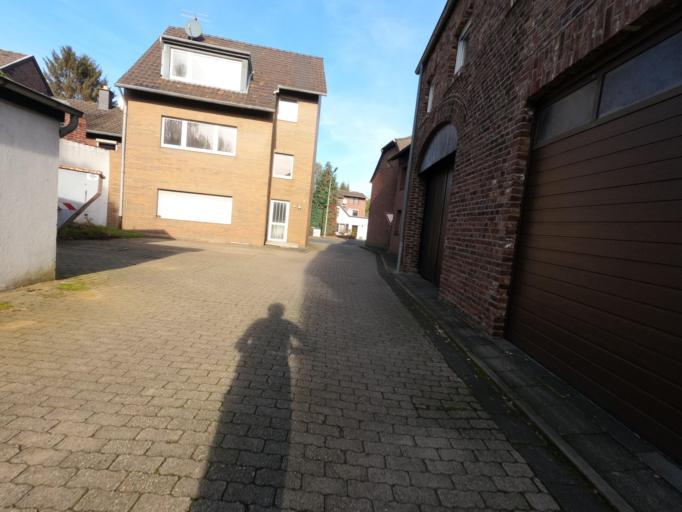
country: DE
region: North Rhine-Westphalia
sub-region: Regierungsbezirk Koln
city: Titz
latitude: 51.0800
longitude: 6.3958
